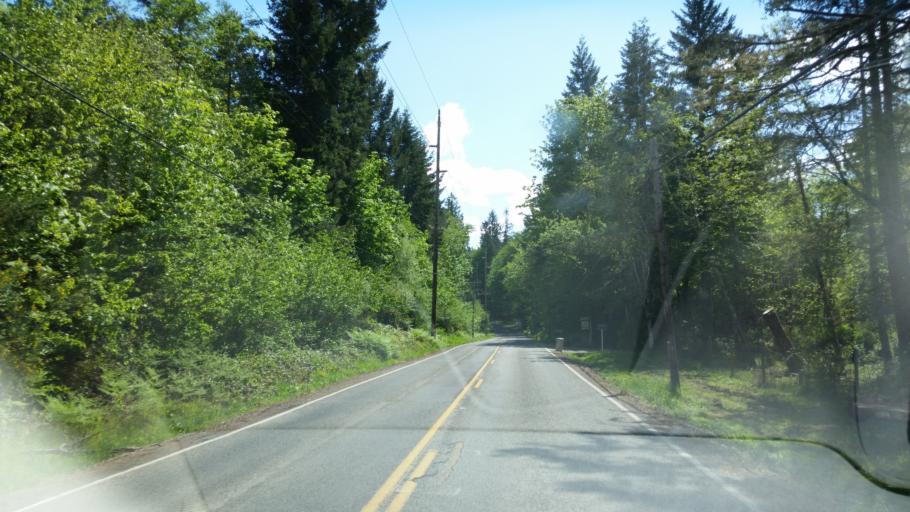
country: US
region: Washington
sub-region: Pierce County
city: Home
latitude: 47.3026
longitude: -122.7698
